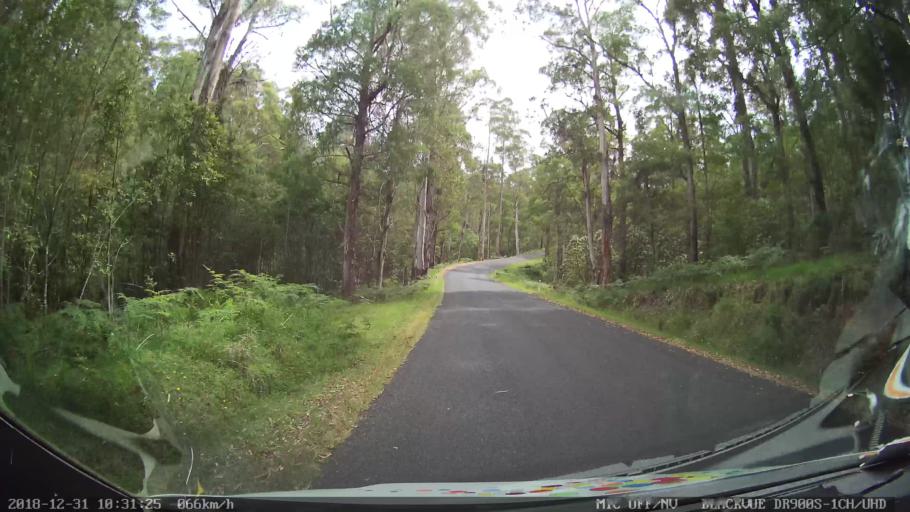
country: AU
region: New South Wales
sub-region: Snowy River
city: Jindabyne
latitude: -36.4577
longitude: 148.1578
